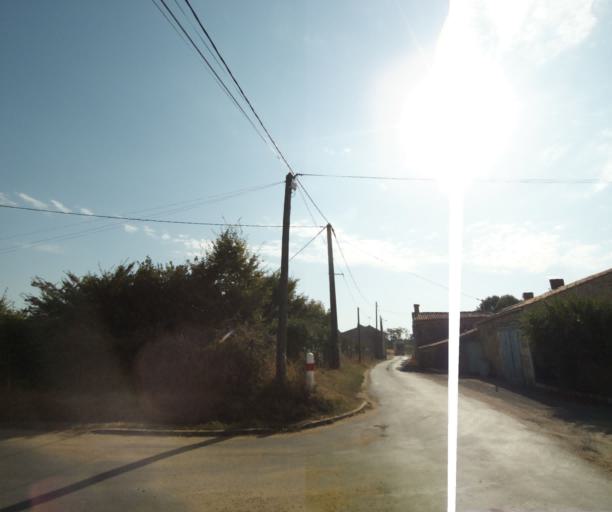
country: FR
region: Poitou-Charentes
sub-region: Departement de la Charente-Maritime
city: Tonnay-Charente
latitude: 45.9622
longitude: -0.8776
